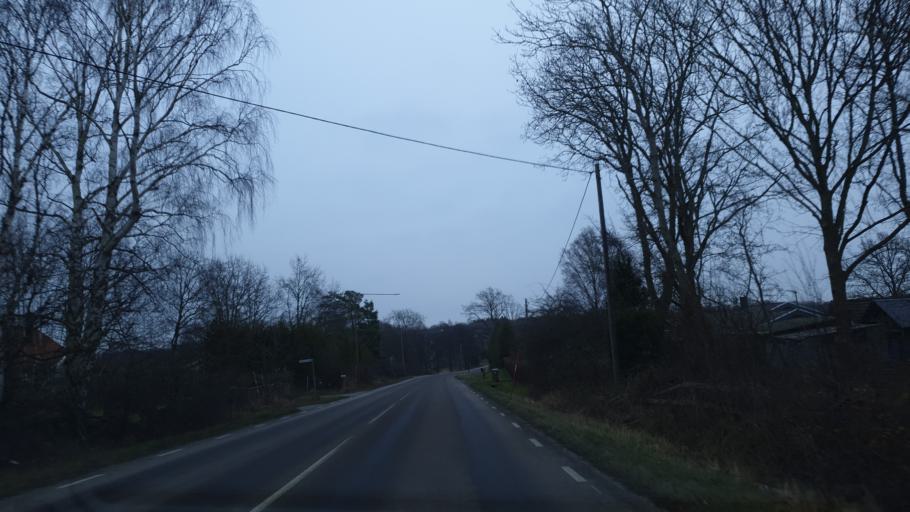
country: SE
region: Blekinge
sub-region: Karlskrona Kommun
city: Sturko
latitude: 56.1121
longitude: 15.7032
